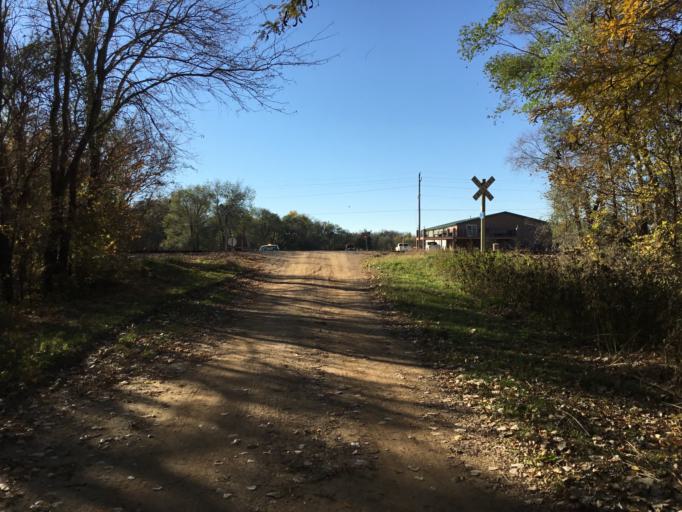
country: US
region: Kansas
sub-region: Lincoln County
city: Lincoln
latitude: 39.0345
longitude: -98.1444
